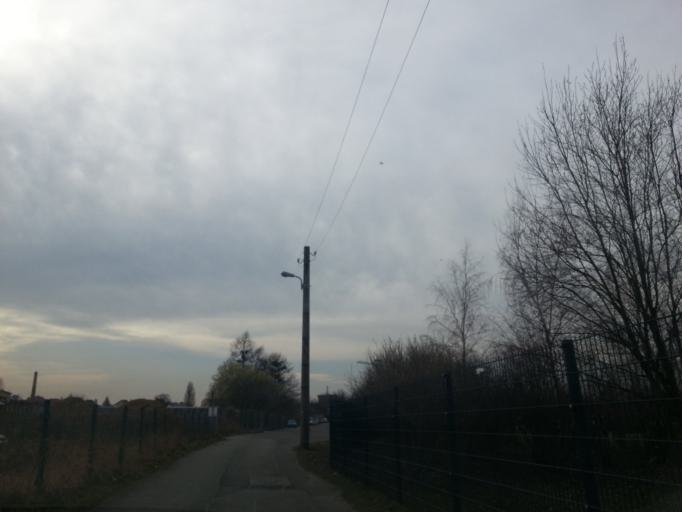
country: DE
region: Saxony
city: Albertstadt
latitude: 51.0863
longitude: 13.7348
